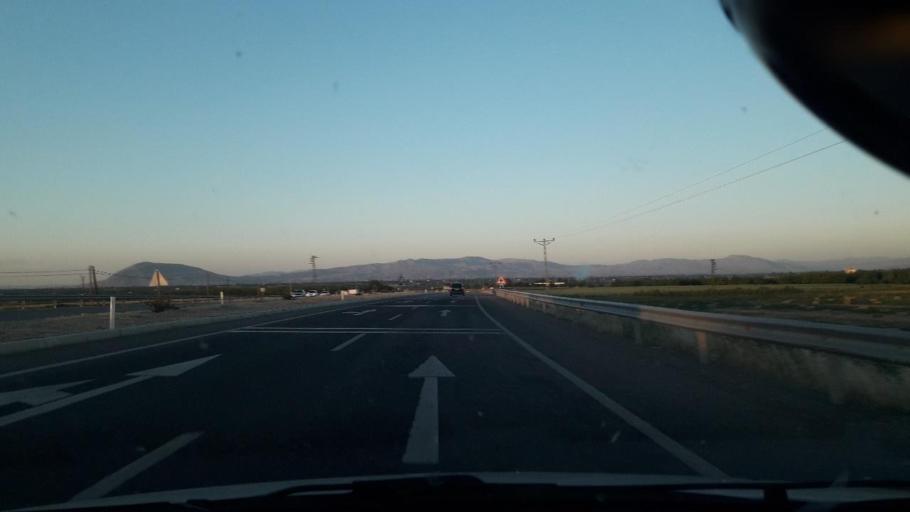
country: TR
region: Malatya
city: Yazihan
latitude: 38.4974
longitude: 38.2232
